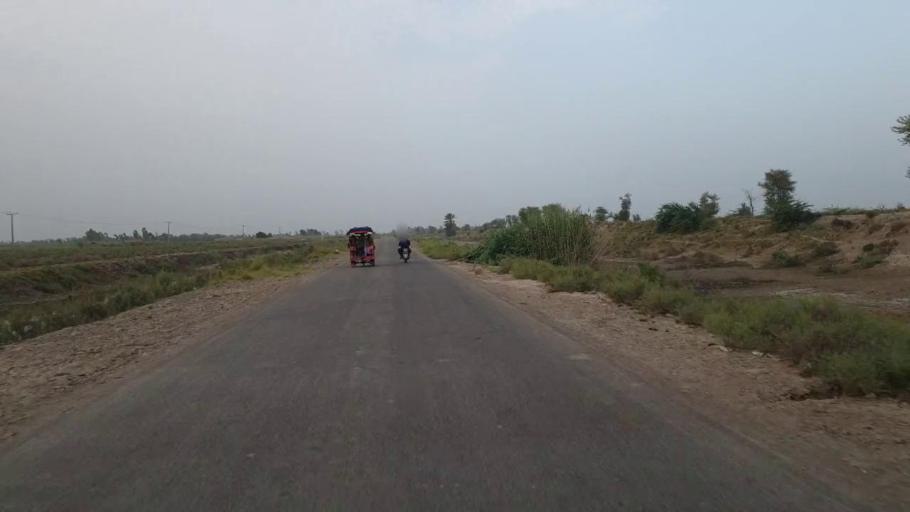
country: PK
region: Sindh
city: Daur
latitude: 26.4460
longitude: 68.2832
